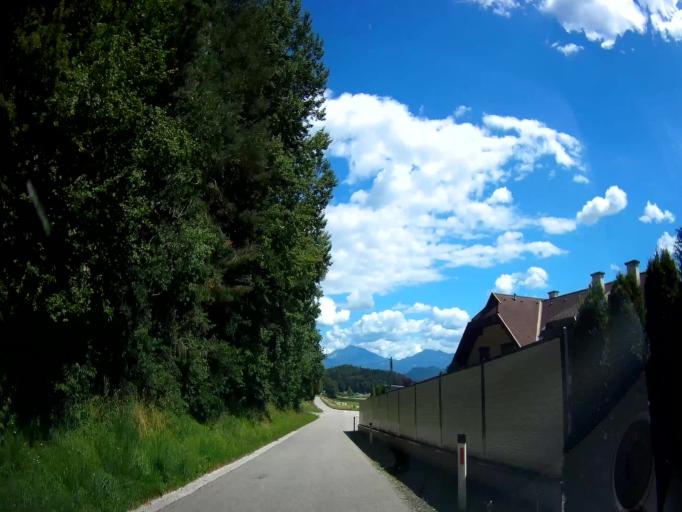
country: AT
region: Carinthia
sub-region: Politischer Bezirk Klagenfurt Land
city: Poggersdorf
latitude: 46.6608
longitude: 14.5390
